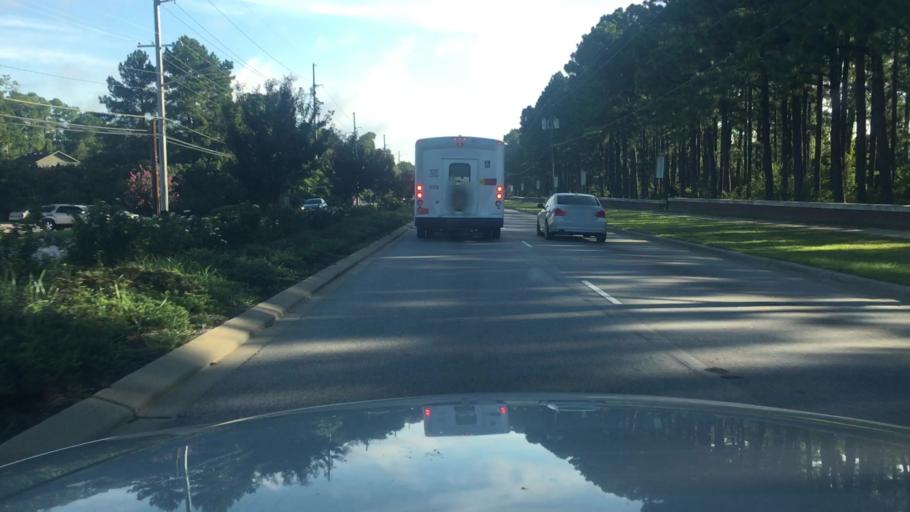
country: US
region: North Carolina
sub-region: Cumberland County
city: Fayetteville
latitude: 35.1337
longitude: -78.8769
